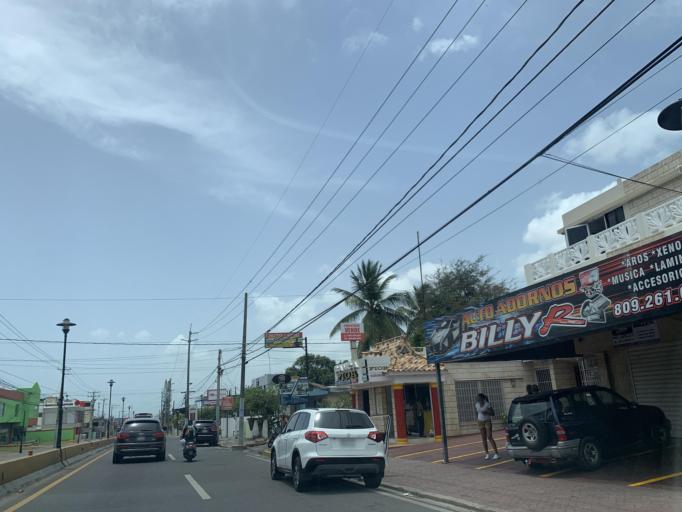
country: DO
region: Puerto Plata
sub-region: Puerto Plata
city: Puerto Plata
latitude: 19.7847
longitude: -70.6827
